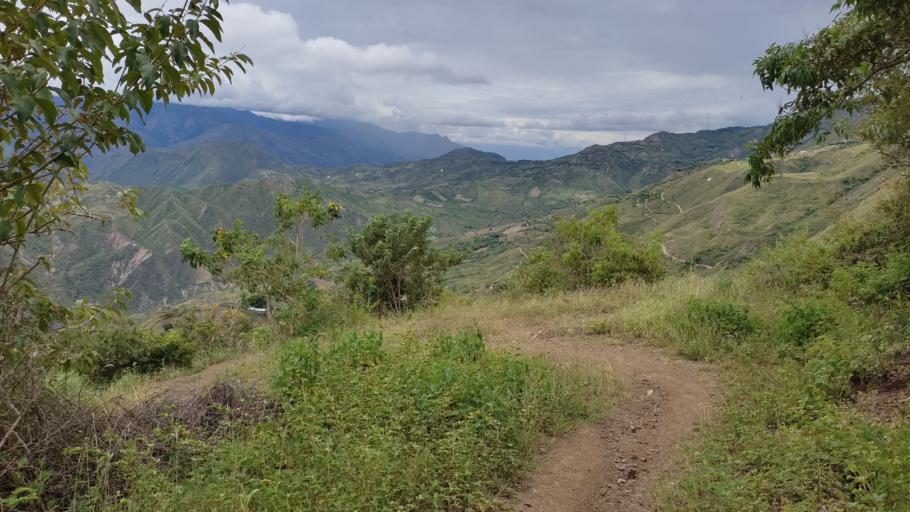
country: CO
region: Narino
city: Taminango
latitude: 1.5442
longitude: -77.3691
